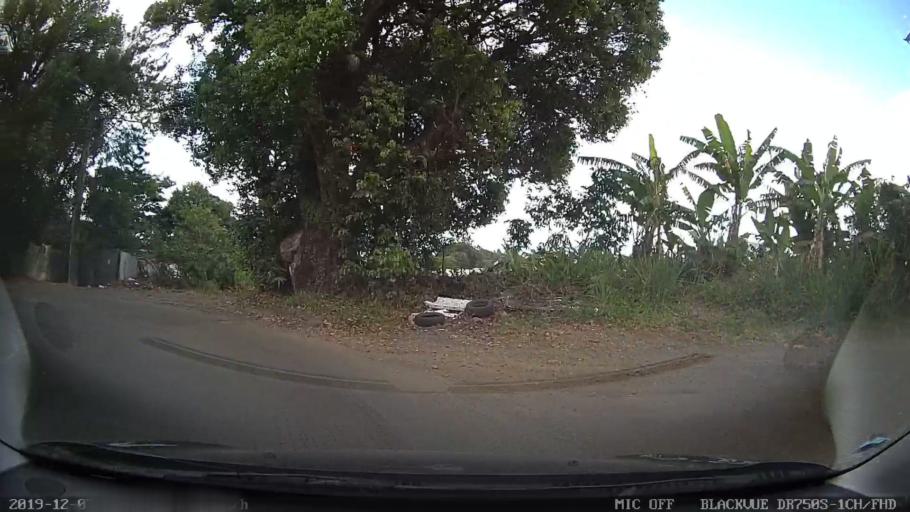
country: RE
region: Reunion
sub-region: Reunion
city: Sainte-Marie
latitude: -20.9359
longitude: 55.5342
